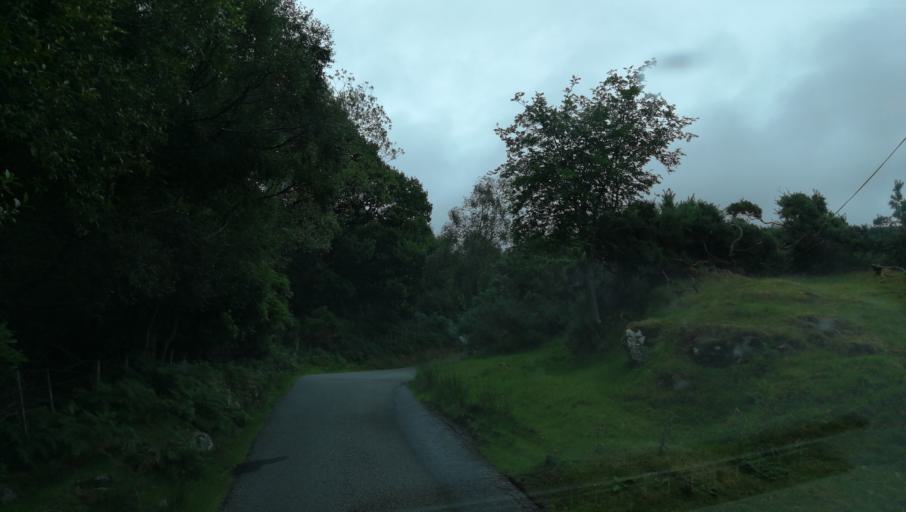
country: GB
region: Scotland
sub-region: Highland
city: Ullapool
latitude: 58.1365
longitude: -5.2544
